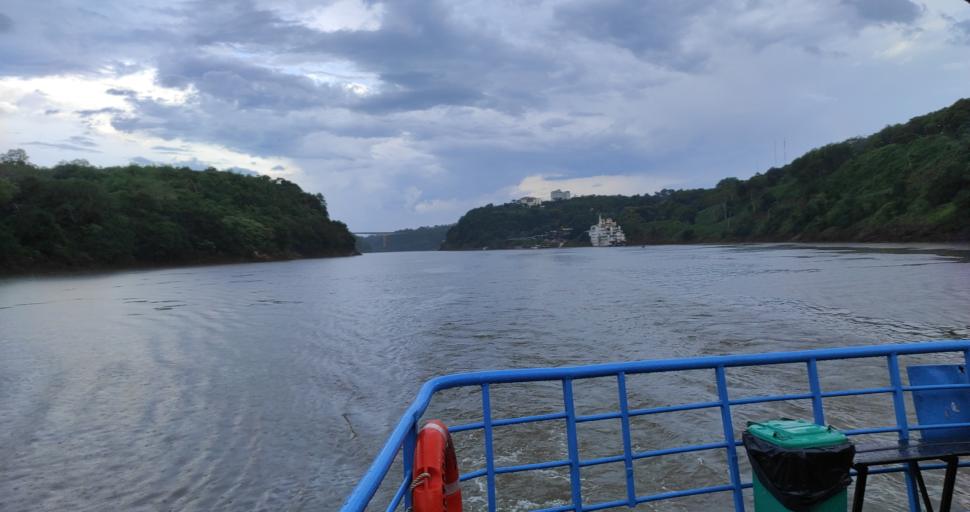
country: AR
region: Misiones
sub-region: Departamento de Iguazu
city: Puerto Iguazu
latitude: -25.5927
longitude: -54.5882
